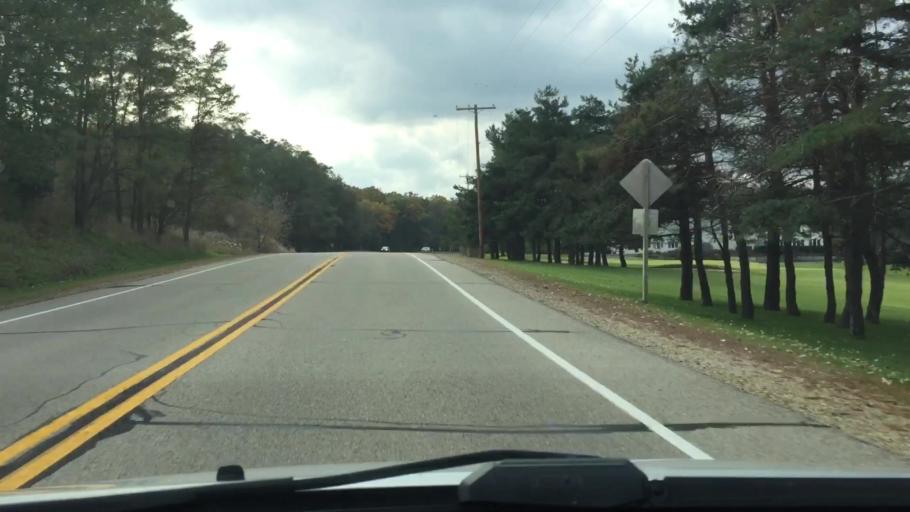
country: US
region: Wisconsin
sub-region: Waukesha County
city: Dousman
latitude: 42.9682
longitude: -88.4738
